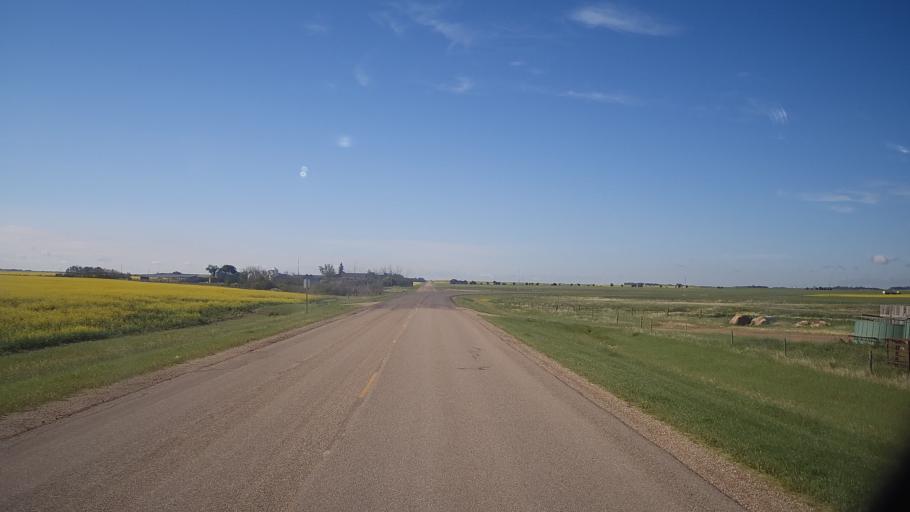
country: CA
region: Saskatchewan
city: Watrous
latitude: 51.6827
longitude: -105.3809
